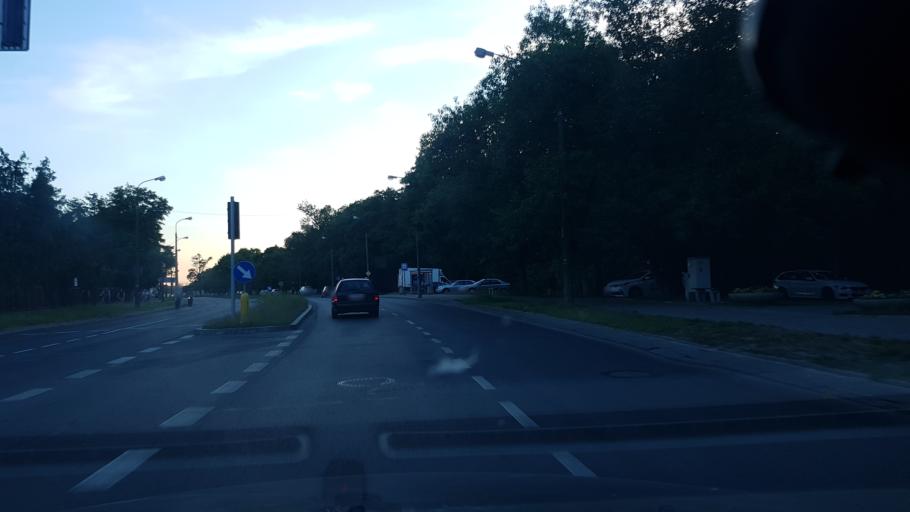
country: PL
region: Masovian Voivodeship
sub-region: Warszawa
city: Wawer
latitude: 52.2070
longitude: 21.1818
